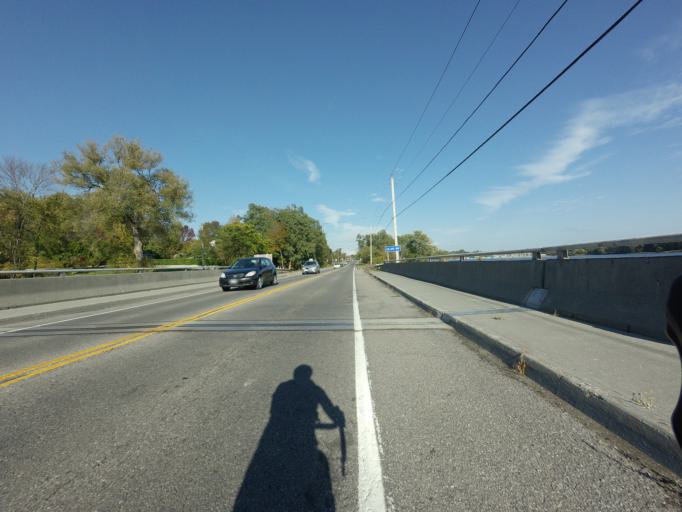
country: CA
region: Ontario
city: Kingston
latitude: 44.2387
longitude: -76.6157
